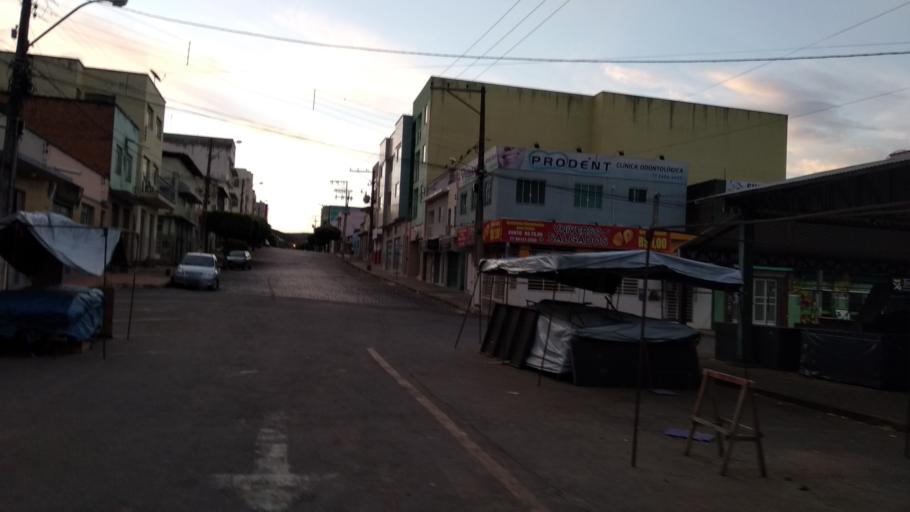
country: BR
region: Bahia
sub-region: Caetite
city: Caetite
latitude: -14.0668
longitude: -42.4910
